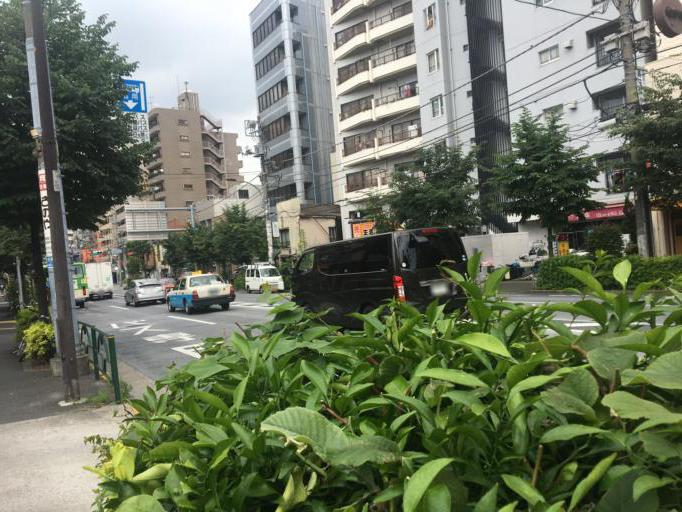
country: JP
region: Tokyo
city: Tokyo
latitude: 35.7355
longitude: 139.7189
